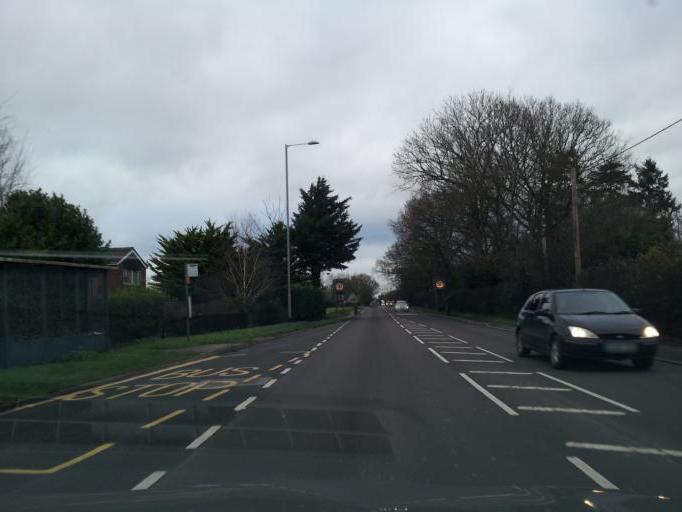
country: GB
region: England
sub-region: Norfolk
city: Long Stratton
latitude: 52.4935
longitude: 1.2380
